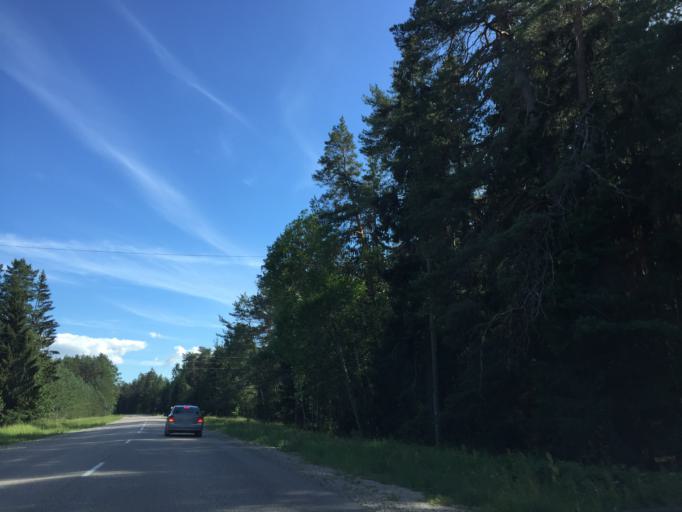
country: LV
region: Ventspils Rajons
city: Piltene
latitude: 57.0898
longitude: 21.7786
